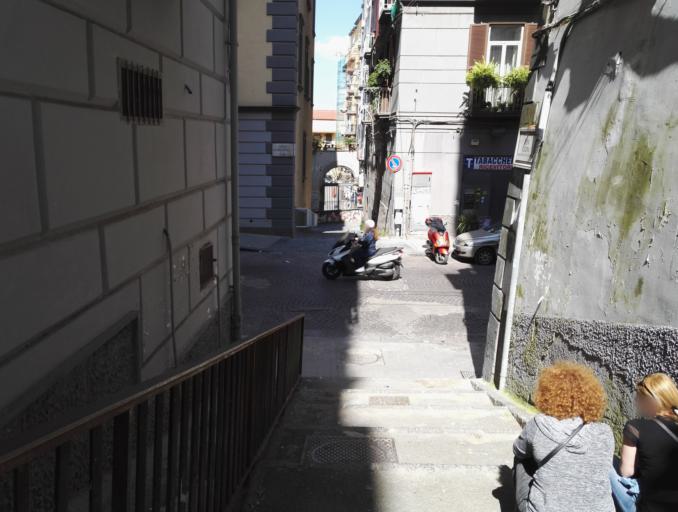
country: IT
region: Campania
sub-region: Provincia di Napoli
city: Napoli
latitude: 40.8477
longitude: 14.2410
